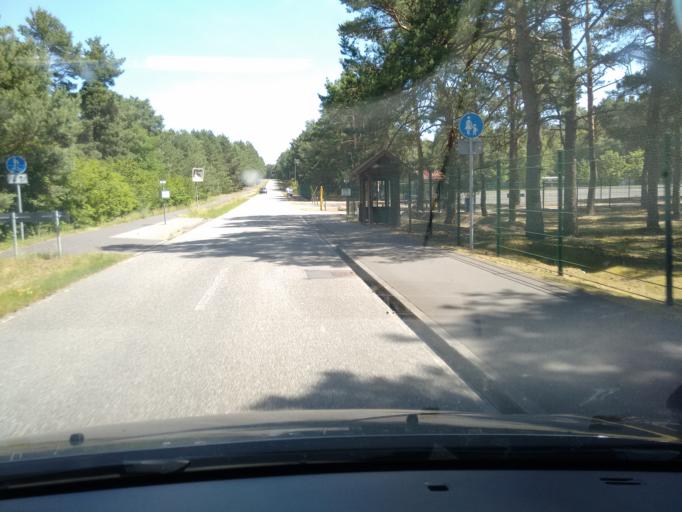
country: DE
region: Brandenburg
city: Mixdorf
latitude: 52.1851
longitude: 14.4437
